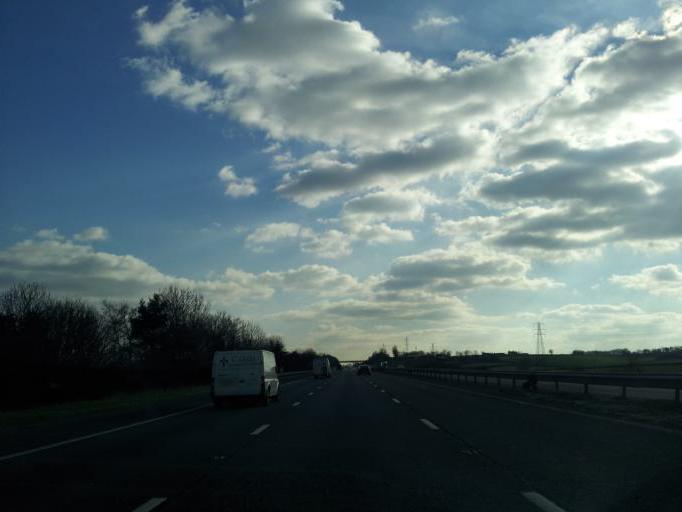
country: GB
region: England
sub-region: Somerset
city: North Petherton
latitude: 51.0752
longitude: -3.0111
